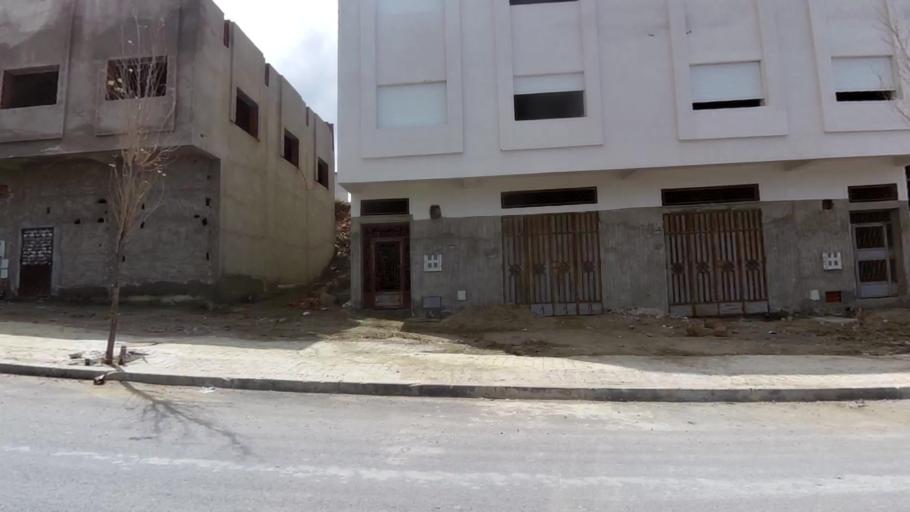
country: MA
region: Tanger-Tetouan
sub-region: Tanger-Assilah
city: Tangier
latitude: 35.7769
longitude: -5.7529
